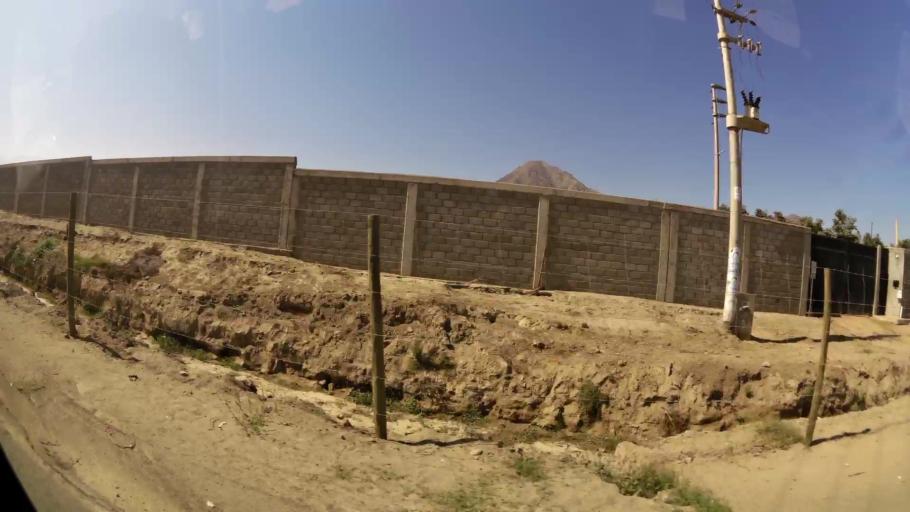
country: PE
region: Ica
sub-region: Provincia de Ica
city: San Juan Bautista
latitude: -13.9522
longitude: -75.6860
